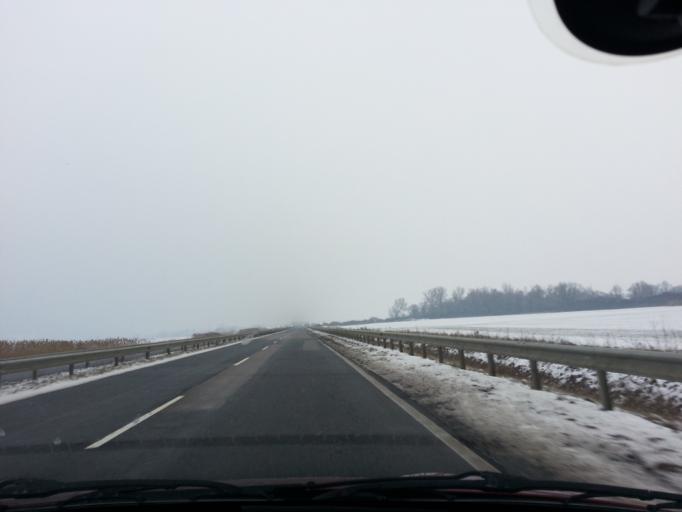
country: HU
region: Nograd
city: Szurdokpuspoki
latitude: 47.8638
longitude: 19.6747
